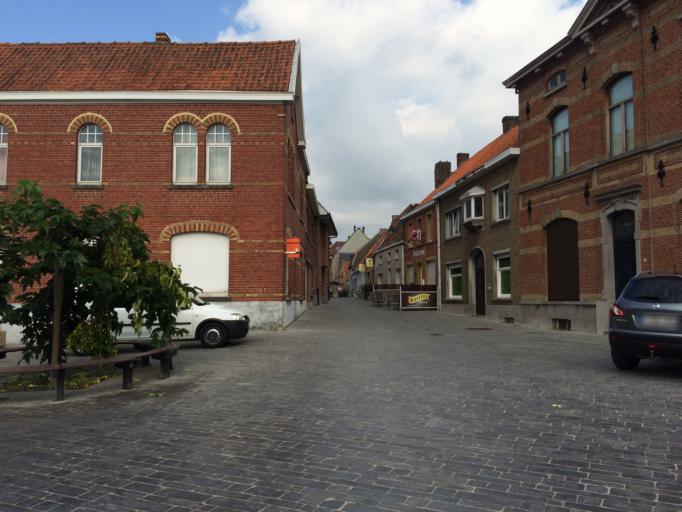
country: BE
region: Flanders
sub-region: Provincie Oost-Vlaanderen
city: Deinze
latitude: 50.9592
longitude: 3.4846
